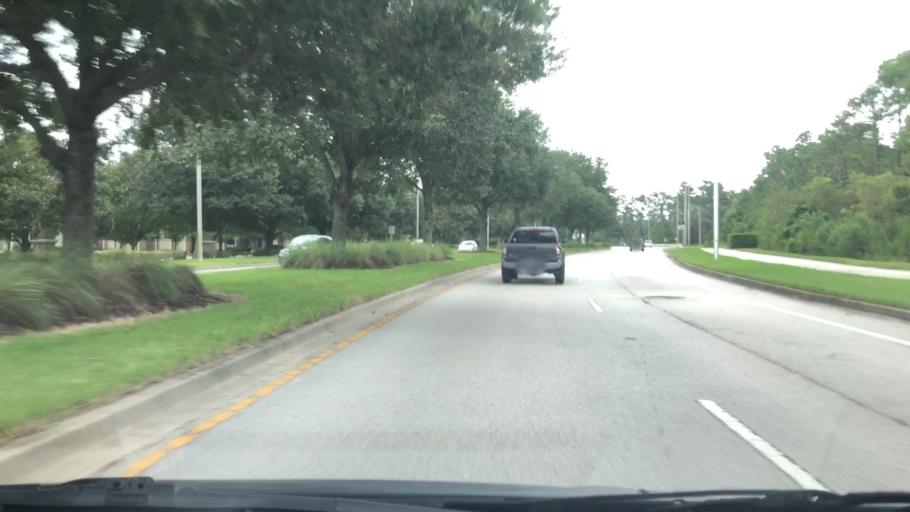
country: US
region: Florida
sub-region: Saint Johns County
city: Fruit Cove
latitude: 30.1260
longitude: -81.5321
